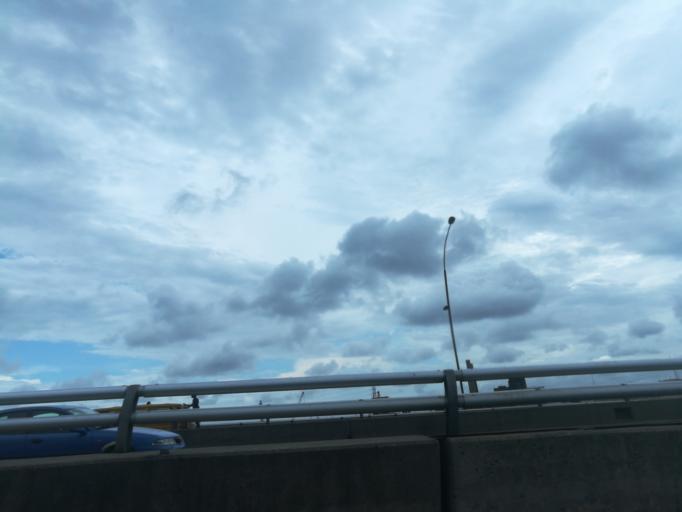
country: NG
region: Lagos
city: Lagos
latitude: 6.4678
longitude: 3.3846
